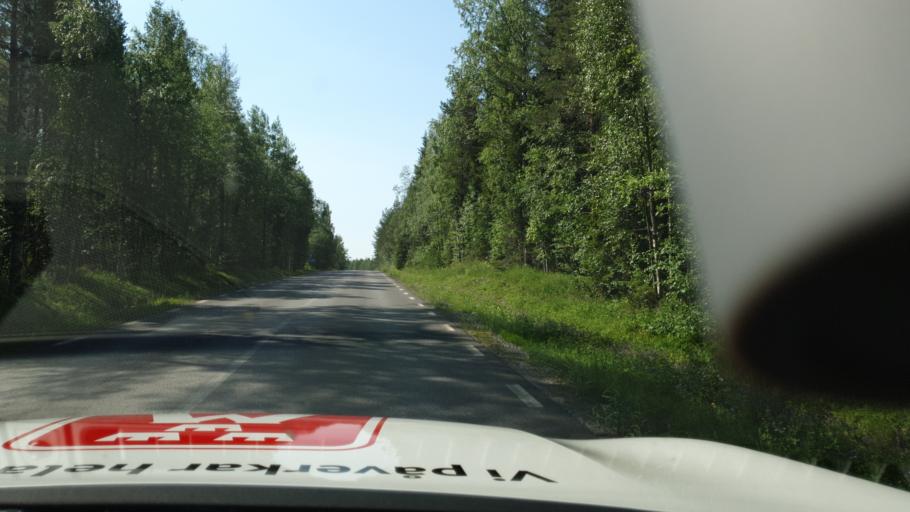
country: SE
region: Vaesterbotten
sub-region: Skelleftea Kommun
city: Langsele
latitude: 64.9719
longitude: 20.0490
